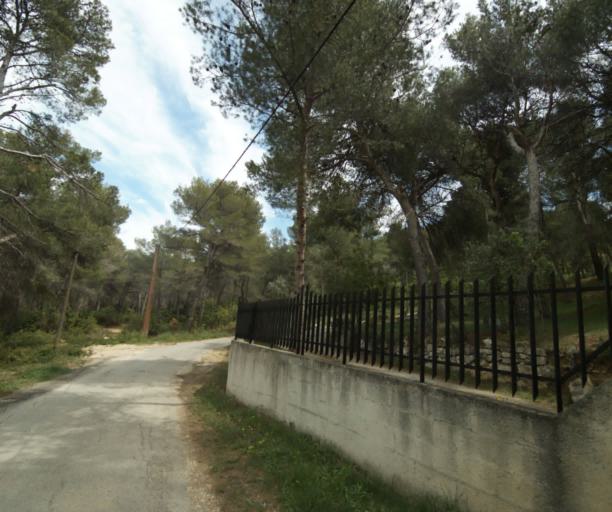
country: FR
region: Provence-Alpes-Cote d'Azur
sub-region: Departement des Bouches-du-Rhone
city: Rognac
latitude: 43.4809
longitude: 5.2429
